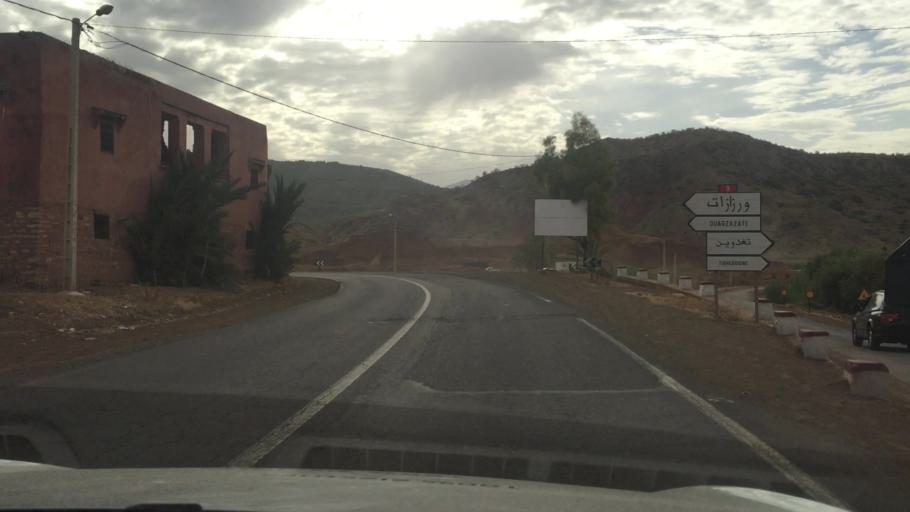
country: MA
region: Marrakech-Tensift-Al Haouz
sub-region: Al-Haouz
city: Touama
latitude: 31.5459
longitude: -7.5724
